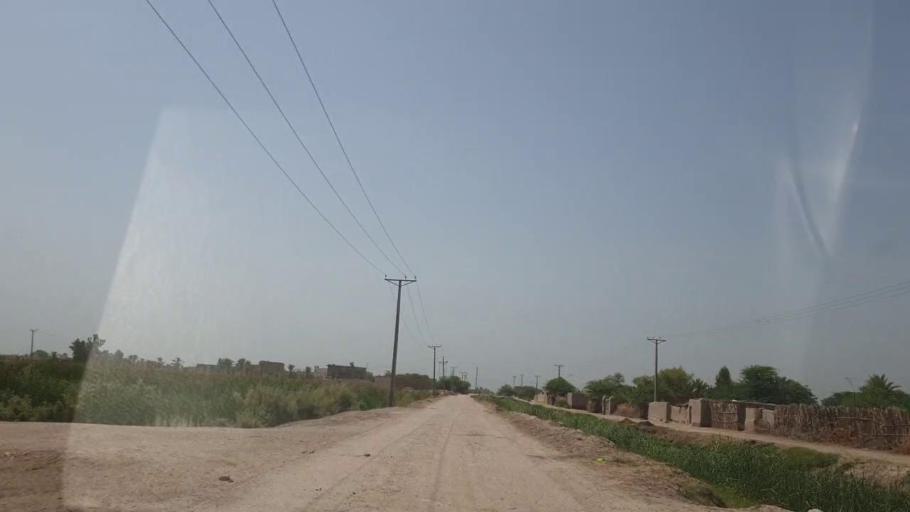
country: PK
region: Sindh
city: Ranipur
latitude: 27.2979
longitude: 68.5454
